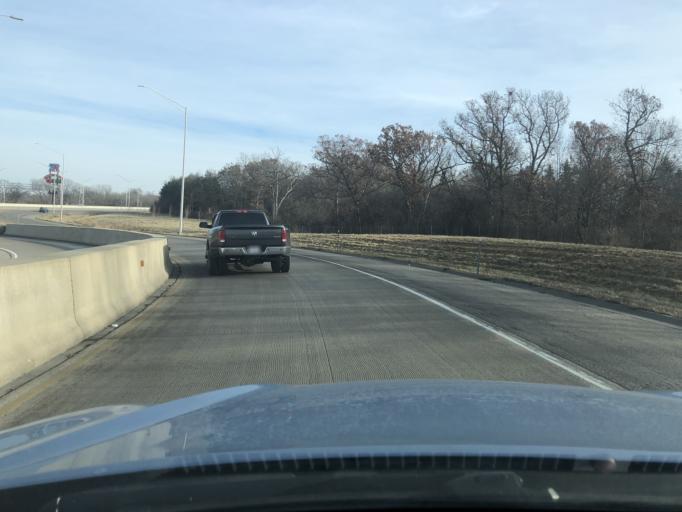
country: US
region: Illinois
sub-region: Kane County
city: Hampshire
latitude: 42.1432
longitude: -88.5144
